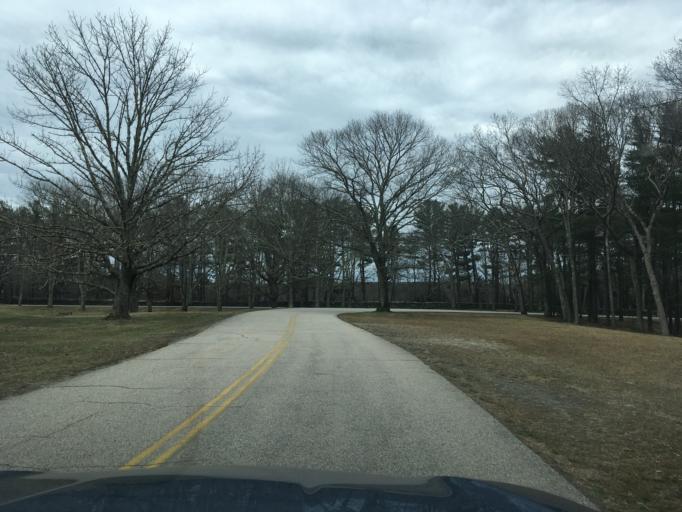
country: US
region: Rhode Island
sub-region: Kent County
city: East Greenwich
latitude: 41.6532
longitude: -71.4417
